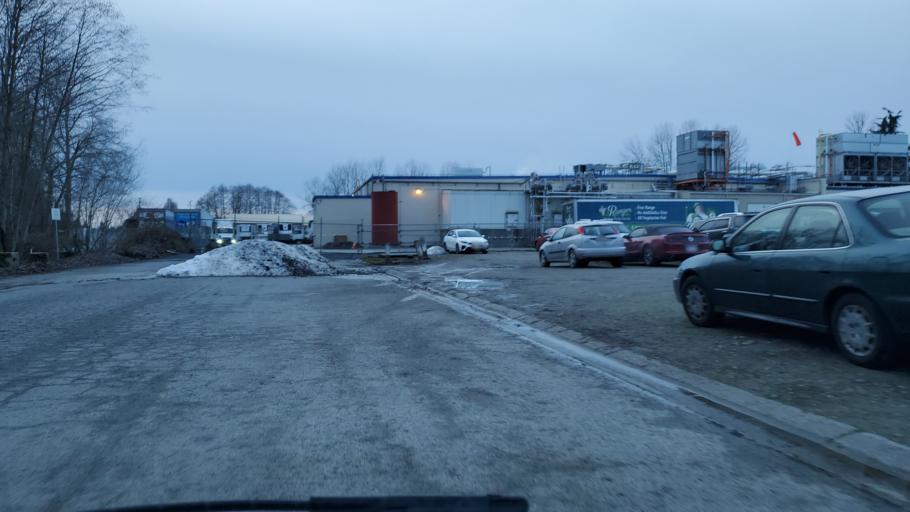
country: US
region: Washington
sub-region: Skagit County
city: Mount Vernon
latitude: 48.4331
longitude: -122.3291
